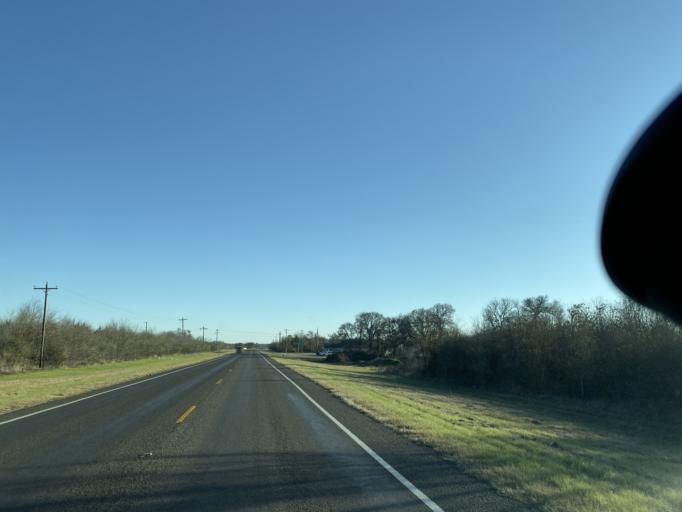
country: US
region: Texas
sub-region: Bastrop County
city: Wyldwood
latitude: 30.1000
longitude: -97.5061
